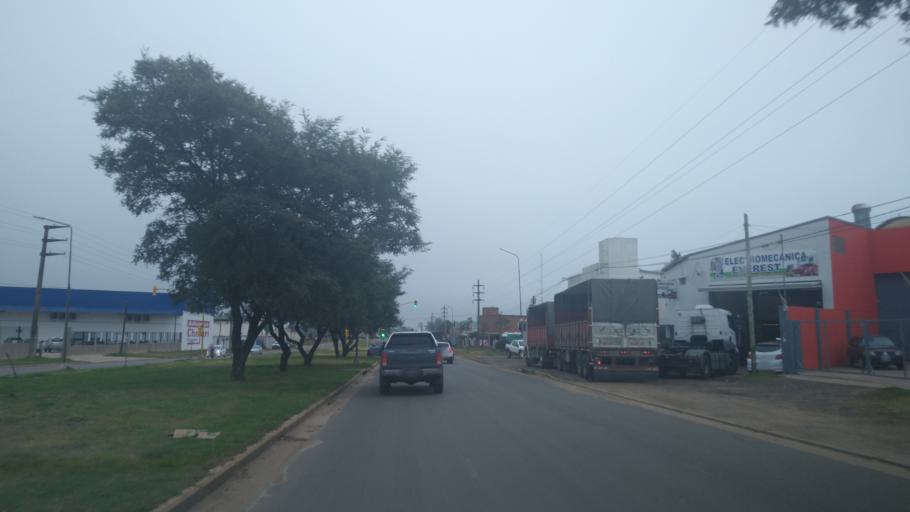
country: AR
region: Entre Rios
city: Chajari
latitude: -30.7618
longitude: -58.0104
